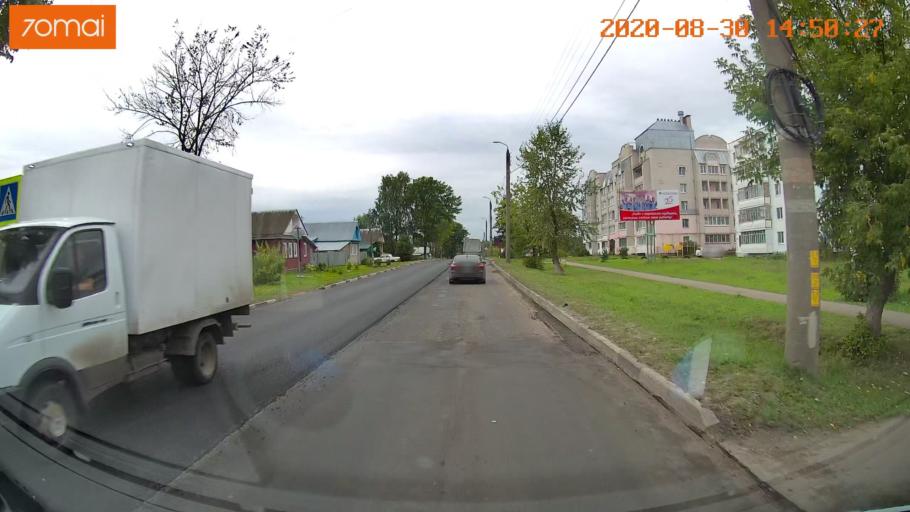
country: RU
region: Ivanovo
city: Kineshma
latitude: 57.4285
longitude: 42.0951
